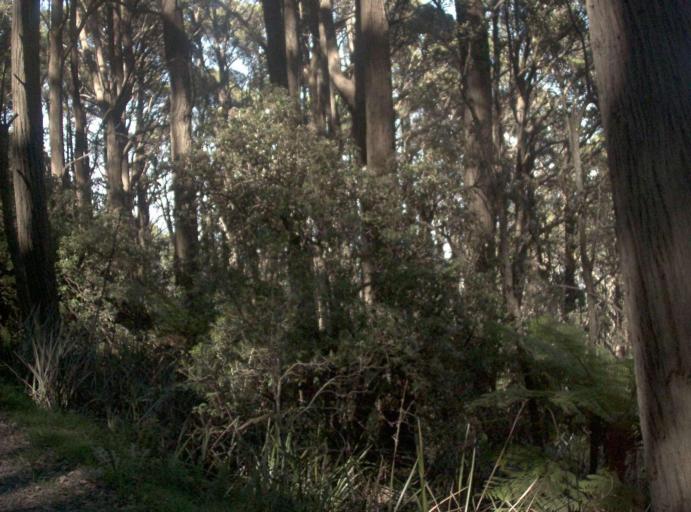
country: AU
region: Victoria
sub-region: Yarra Ranges
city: Millgrove
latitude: -37.7213
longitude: 145.6133
